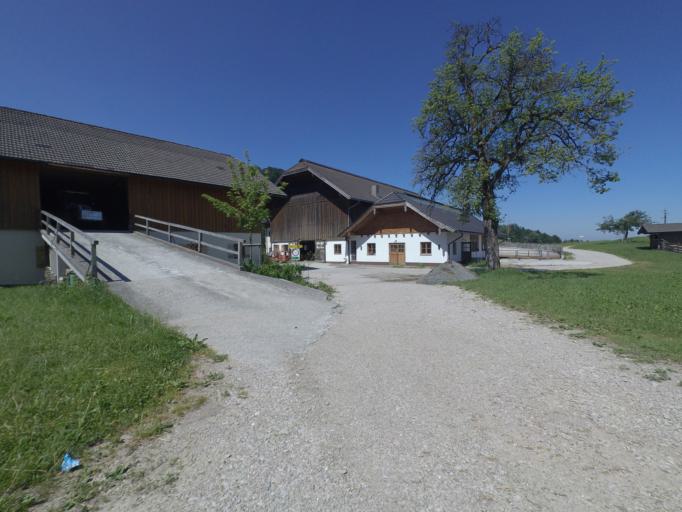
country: AT
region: Salzburg
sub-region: Politischer Bezirk Salzburg-Umgebung
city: Elsbethen
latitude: 47.7613
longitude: 13.1078
